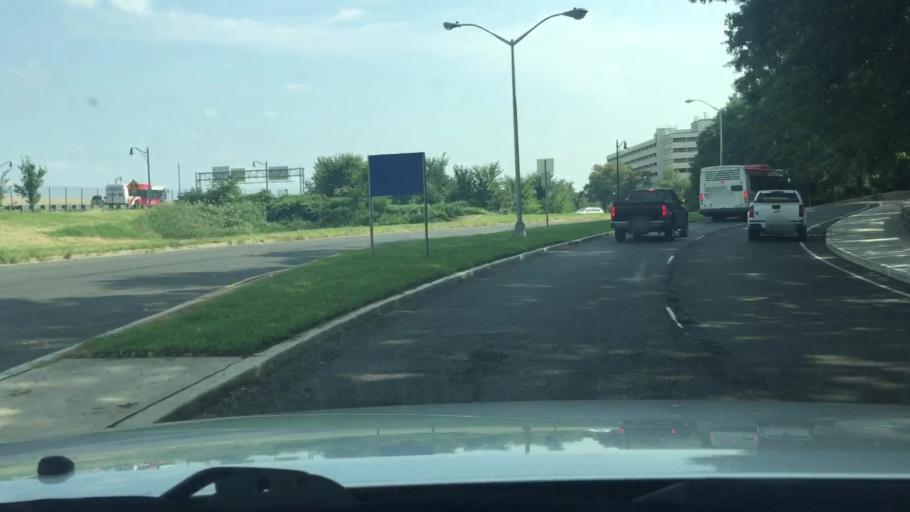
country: US
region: New Jersey
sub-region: Middlesex County
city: New Brunswick
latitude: 40.4991
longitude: -74.4413
